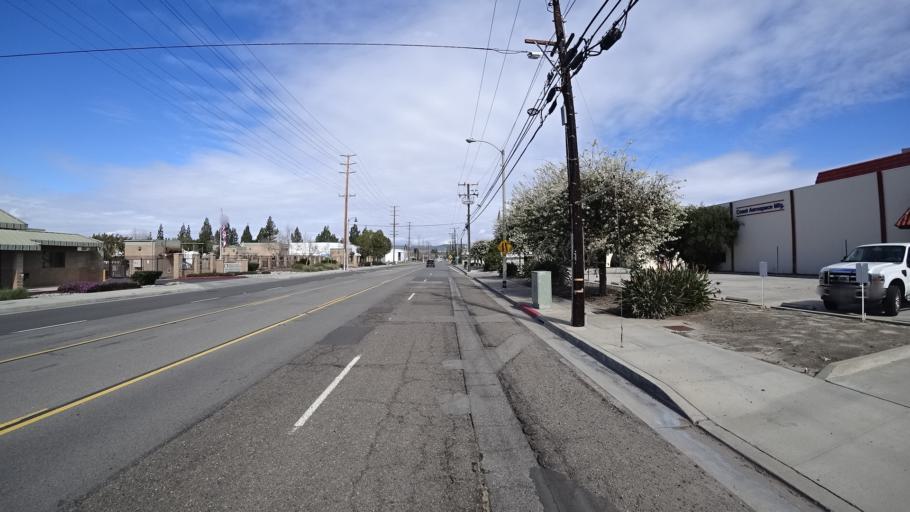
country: US
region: California
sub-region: Orange County
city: Yorba Linda
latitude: 33.8627
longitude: -117.8259
